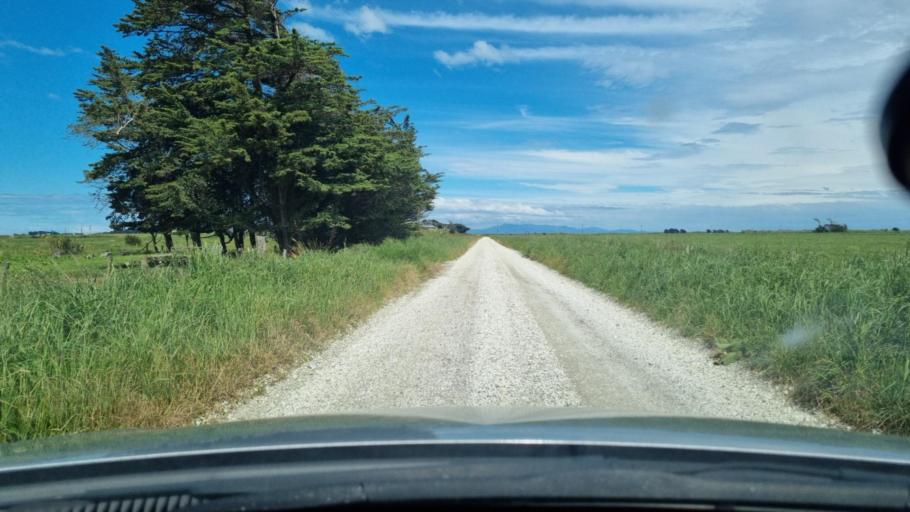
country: NZ
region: Southland
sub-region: Invercargill City
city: Invercargill
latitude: -46.3870
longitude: 168.2636
